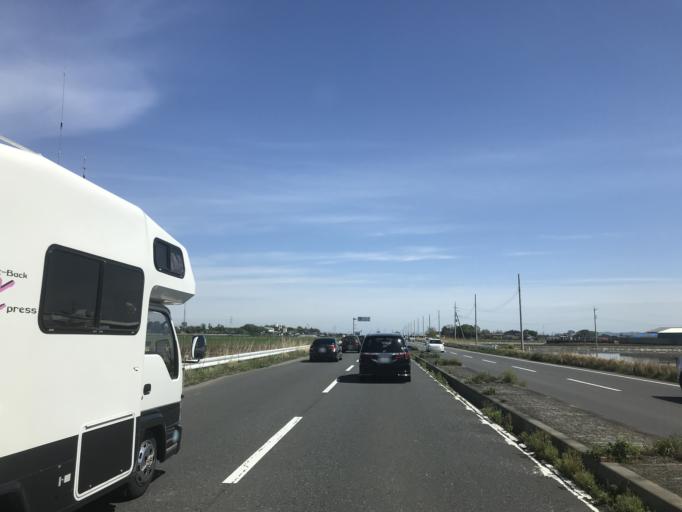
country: JP
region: Ibaraki
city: Shimodate
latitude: 36.2082
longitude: 139.9848
